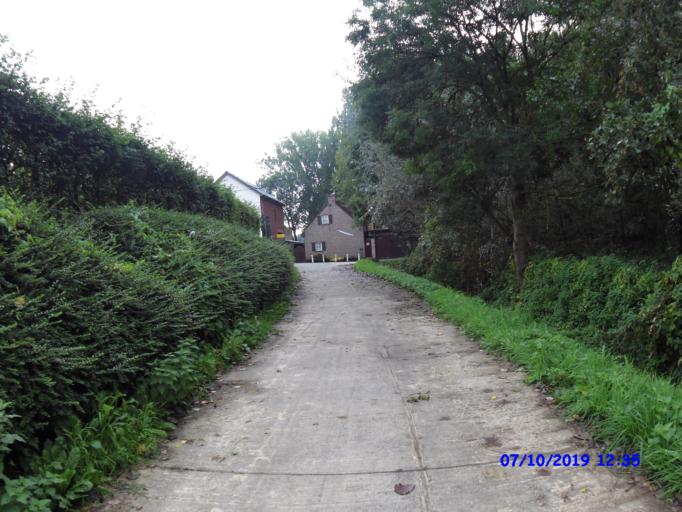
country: BE
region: Flanders
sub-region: Provincie Oost-Vlaanderen
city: Oosterzele
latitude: 50.9300
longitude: 3.7829
